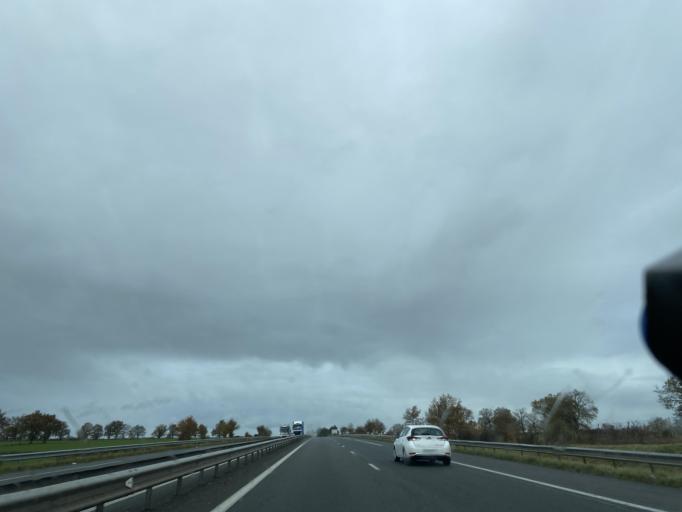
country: FR
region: Auvergne
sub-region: Departement de l'Allier
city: Doyet
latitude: 46.3744
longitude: 2.7374
